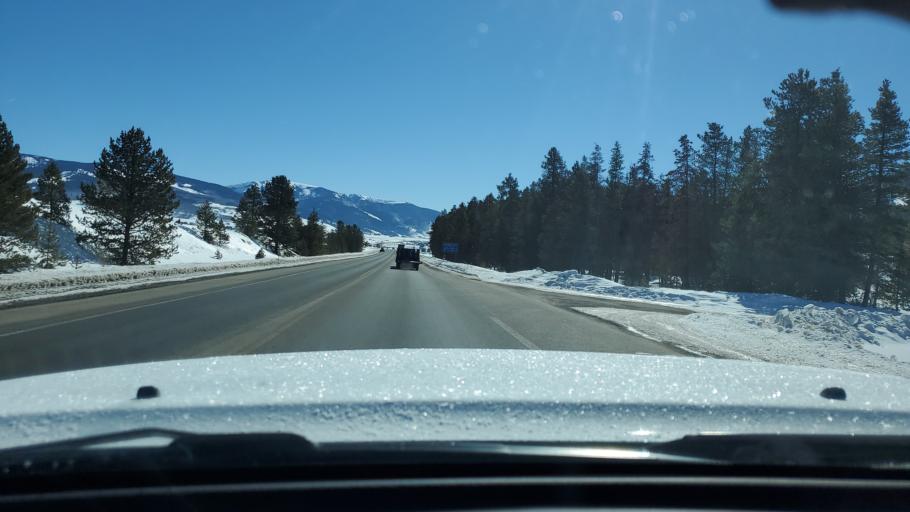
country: US
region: Colorado
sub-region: Gunnison County
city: Crested Butte
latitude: 38.8613
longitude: -106.9729
